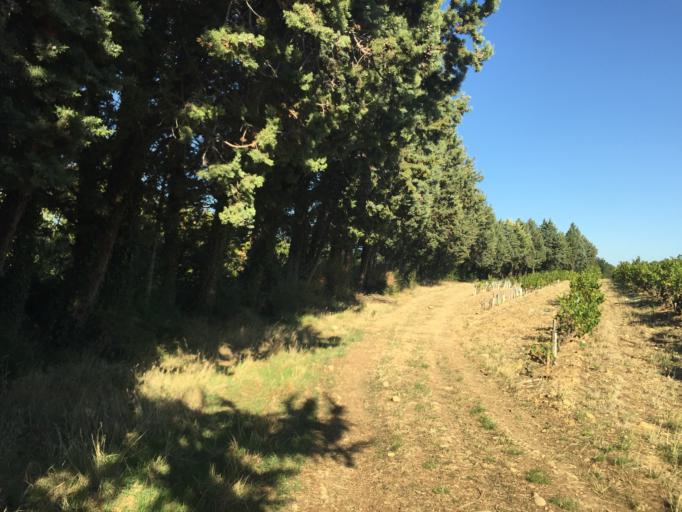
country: FR
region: Provence-Alpes-Cote d'Azur
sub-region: Departement du Vaucluse
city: Chateauneuf-du-Pape
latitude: 44.0577
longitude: 4.8430
